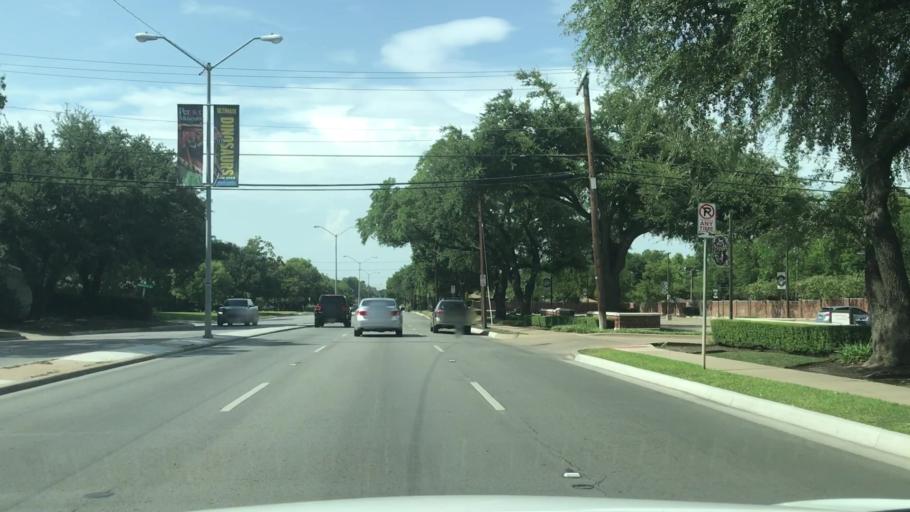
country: US
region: Texas
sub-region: Dallas County
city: Highland Park
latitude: 32.8394
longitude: -96.7529
